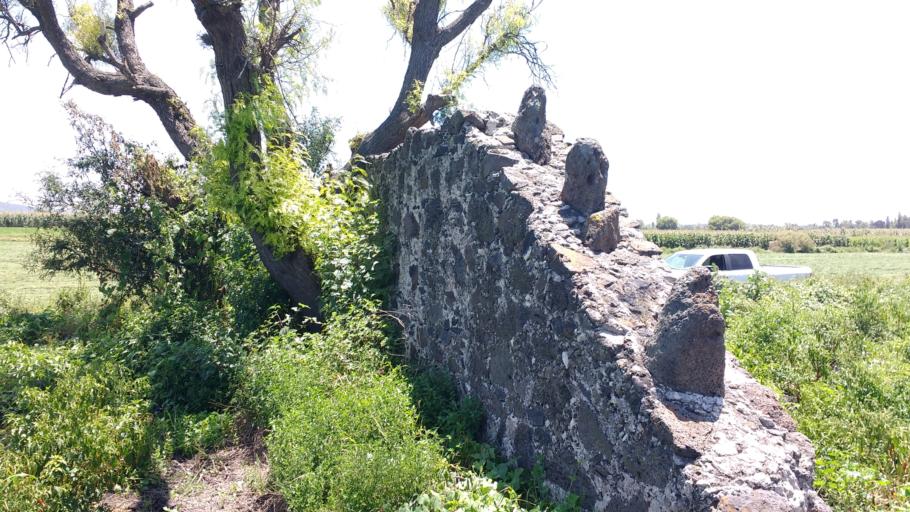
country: MX
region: Hidalgo
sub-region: Tezontepec de Aldama
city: Tenango
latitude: 20.2395
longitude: -99.2547
